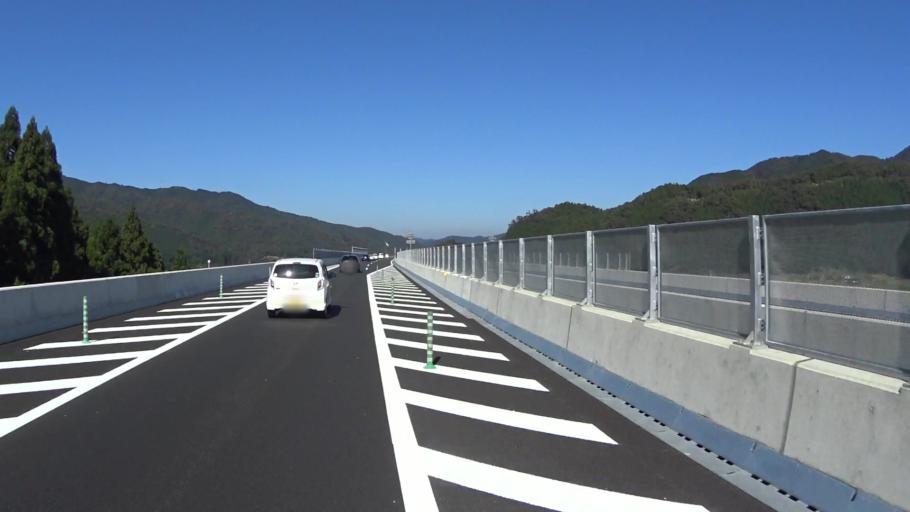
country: JP
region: Kyoto
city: Ayabe
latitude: 35.2728
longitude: 135.3410
